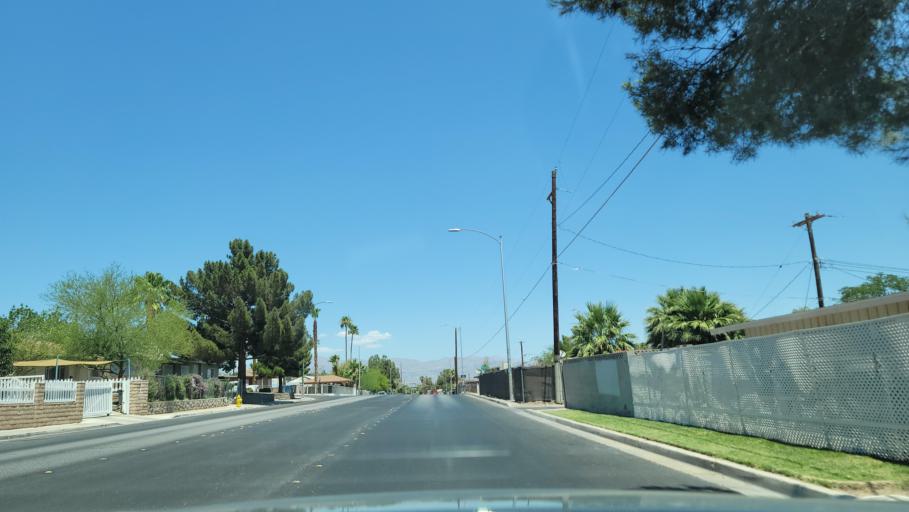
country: US
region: Nevada
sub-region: Clark County
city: Las Vegas
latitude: 36.1703
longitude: -115.1251
